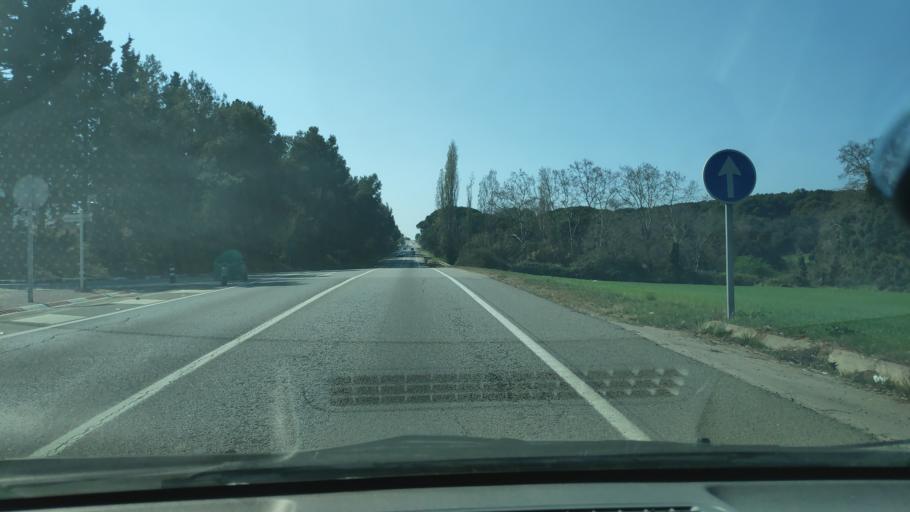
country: ES
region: Catalonia
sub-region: Provincia de Barcelona
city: Polinya
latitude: 41.5327
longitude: 2.1493
